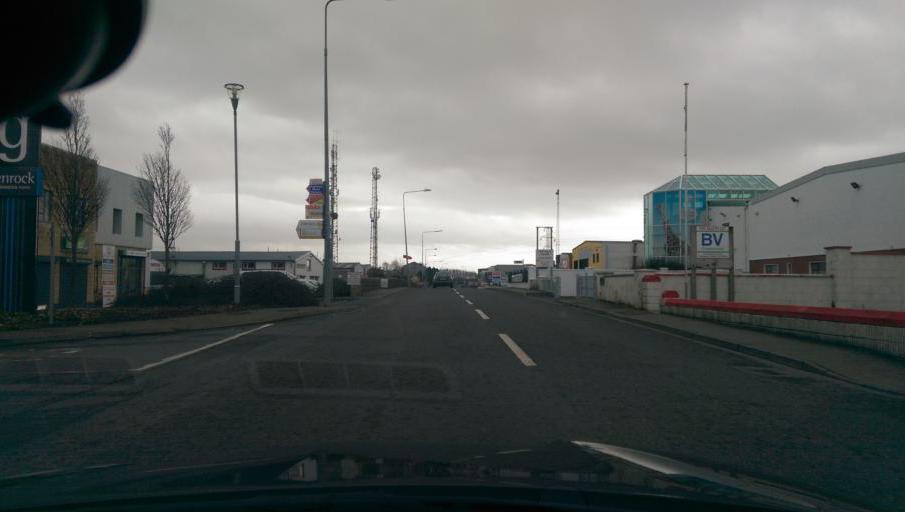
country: IE
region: Connaught
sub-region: County Galway
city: Gaillimh
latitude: 53.2918
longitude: -9.0163
